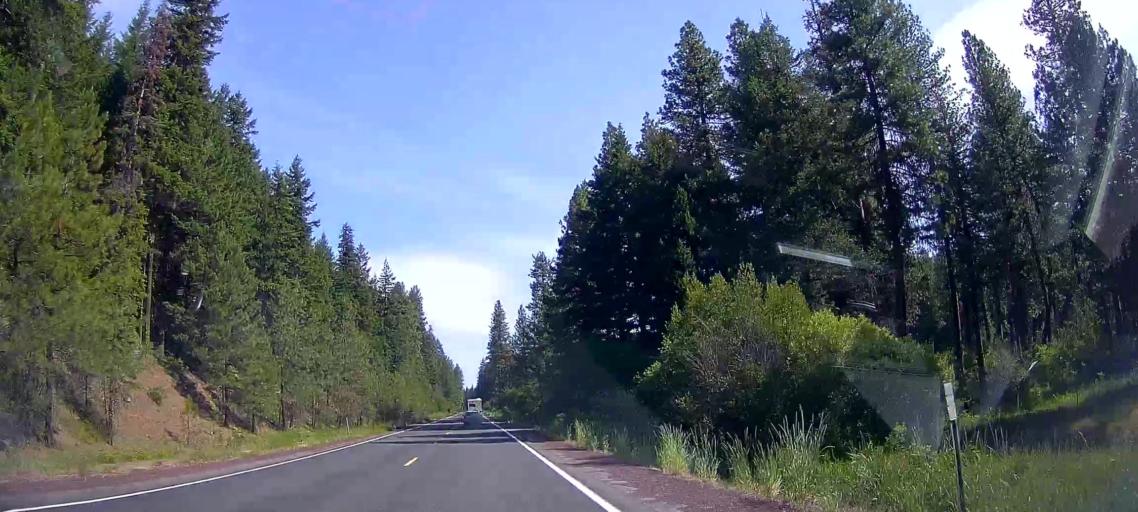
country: US
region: Oregon
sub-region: Jefferson County
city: Warm Springs
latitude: 45.0376
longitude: -121.5105
